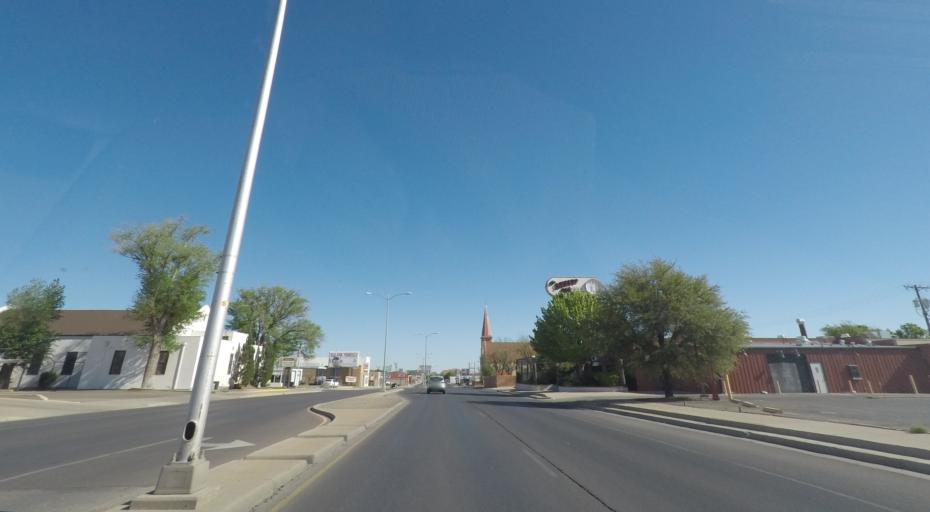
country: US
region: New Mexico
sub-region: Chaves County
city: Roswell
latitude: 33.3838
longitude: -104.5227
